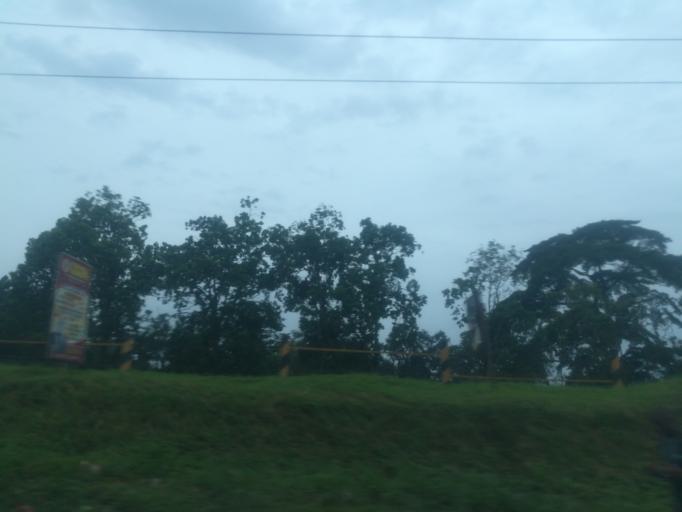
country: NG
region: Oyo
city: Ibadan
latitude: 7.3935
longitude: 3.9697
